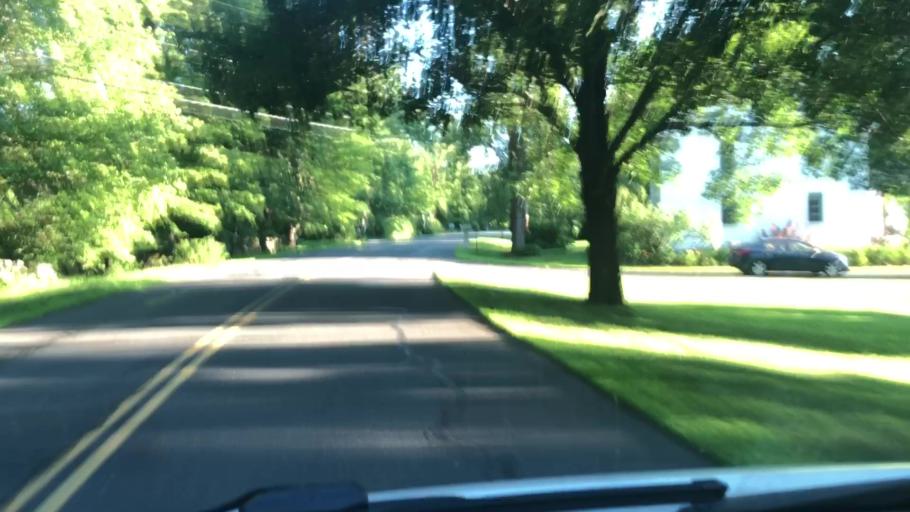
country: US
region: Massachusetts
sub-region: Hampshire County
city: Williamsburg
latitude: 42.3652
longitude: -72.7240
